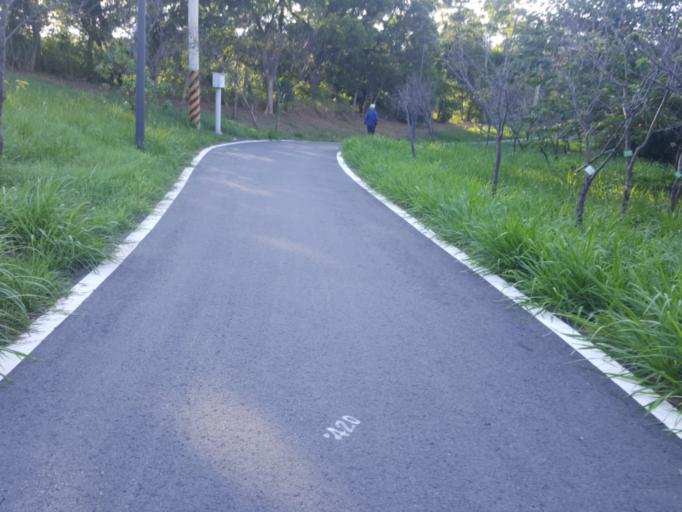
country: TW
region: Taiwan
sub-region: Hsinchu
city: Hsinchu
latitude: 24.7671
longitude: 120.9343
